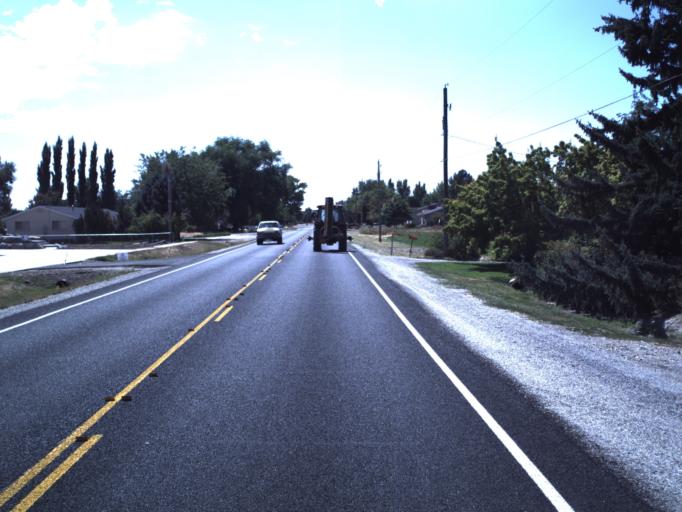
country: US
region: Utah
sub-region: Box Elder County
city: Honeyville
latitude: 41.6202
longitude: -112.1269
